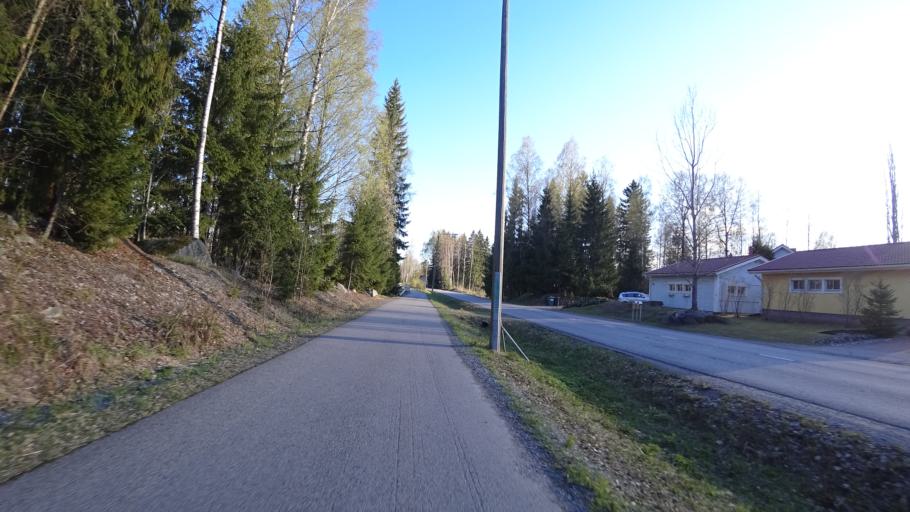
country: FI
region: Pirkanmaa
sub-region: Tampere
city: Yloejaervi
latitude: 61.5111
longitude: 23.5949
